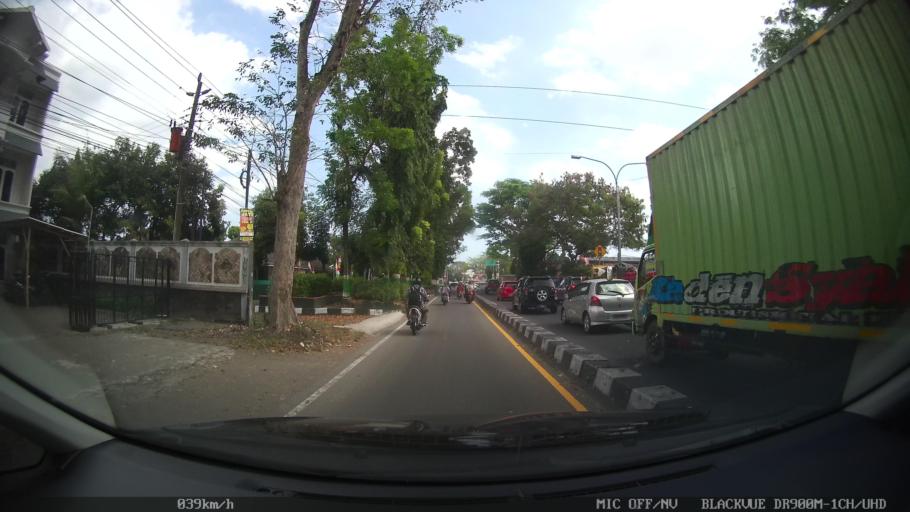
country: ID
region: Daerah Istimewa Yogyakarta
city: Gamping Lor
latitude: -7.7751
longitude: 110.3325
